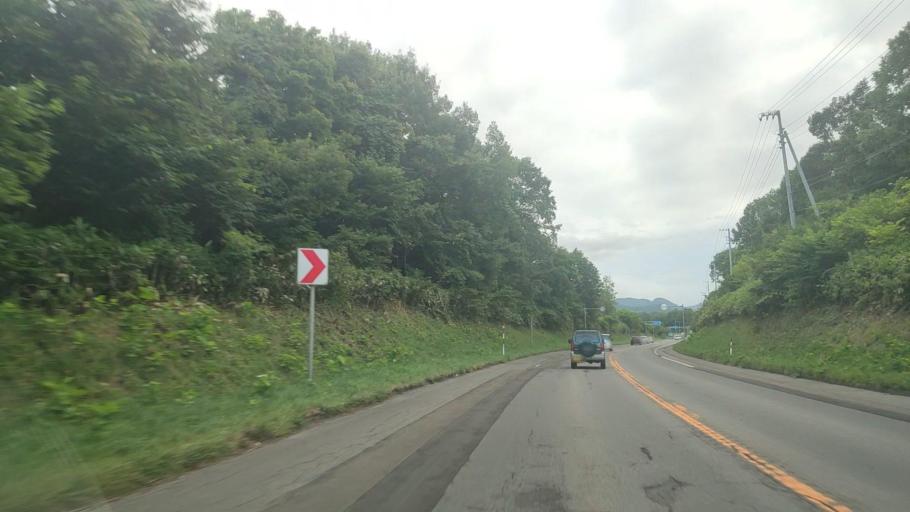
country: JP
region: Hokkaido
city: Nanae
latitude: 42.0645
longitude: 140.6022
